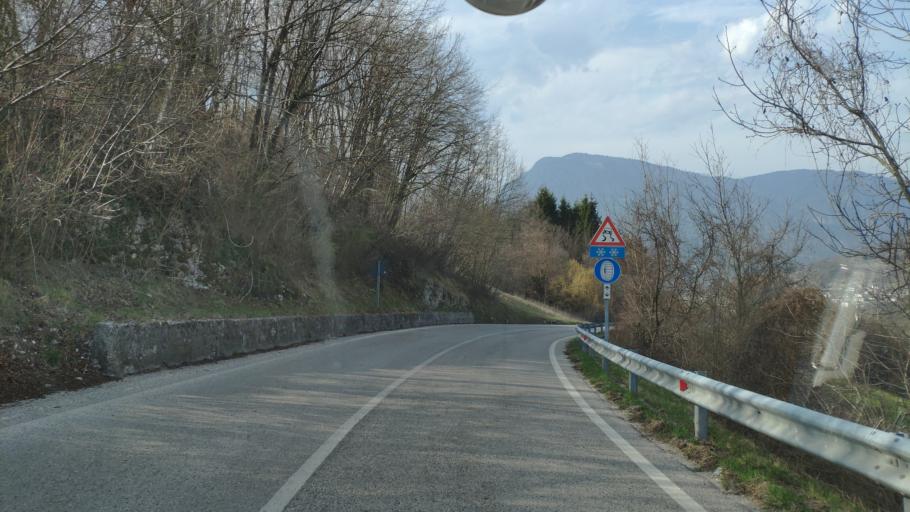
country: IT
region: Veneto
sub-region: Provincia di Vicenza
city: Enego
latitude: 45.9453
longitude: 11.7213
